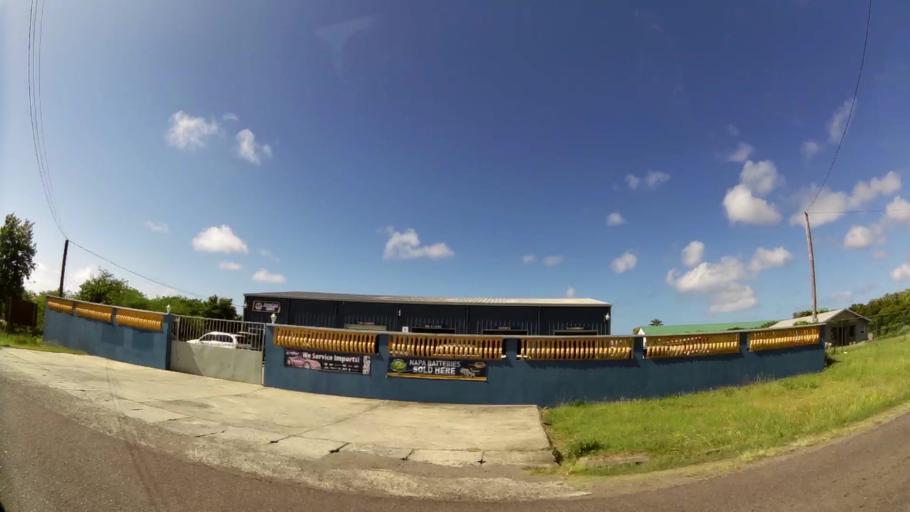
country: LC
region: Laborie Quarter
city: Laborie
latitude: 13.7379
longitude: -60.9700
